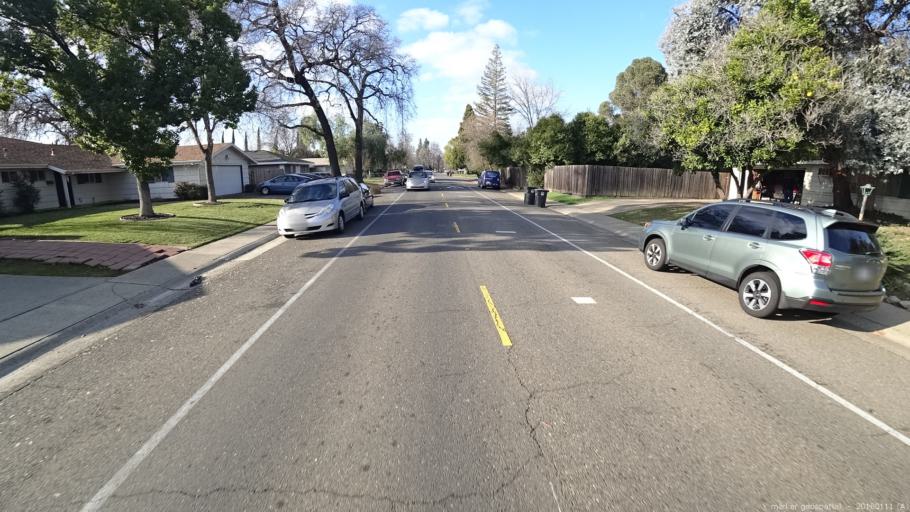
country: US
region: California
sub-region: Sacramento County
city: Rancho Cordova
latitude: 38.6035
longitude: -121.3001
